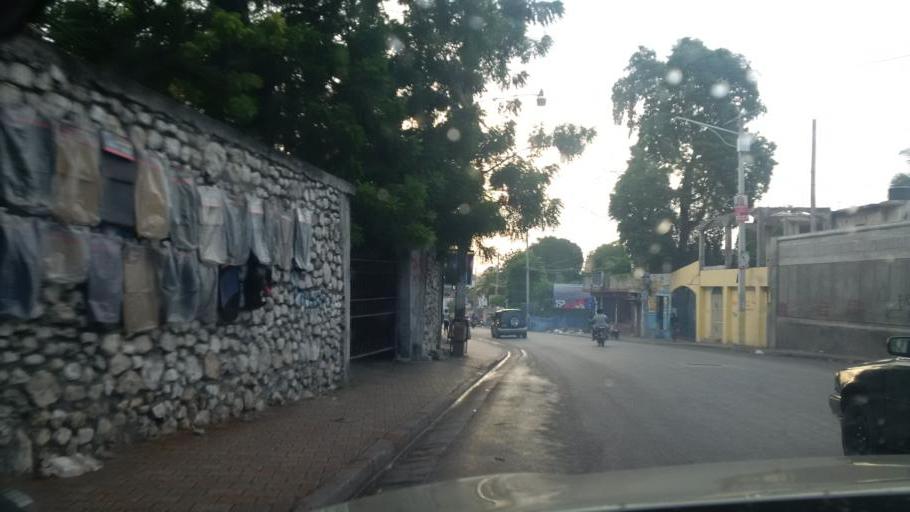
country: HT
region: Ouest
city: Port-au-Prince
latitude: 18.5389
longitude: -72.3298
